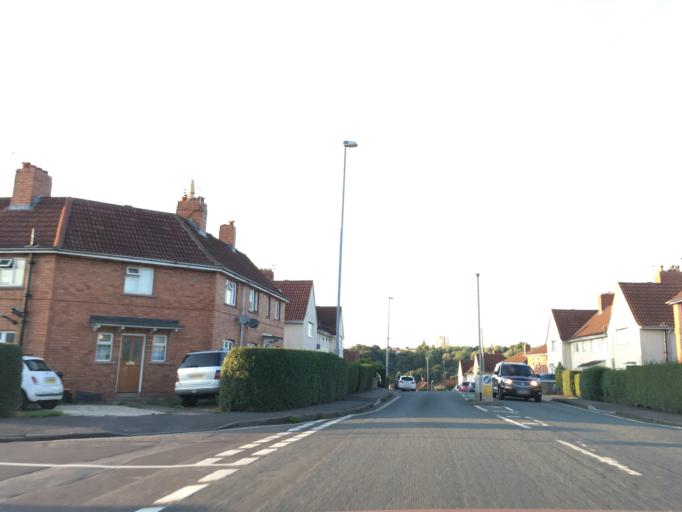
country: GB
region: England
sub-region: South Gloucestershire
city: Kingswood
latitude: 51.4505
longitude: -2.5416
